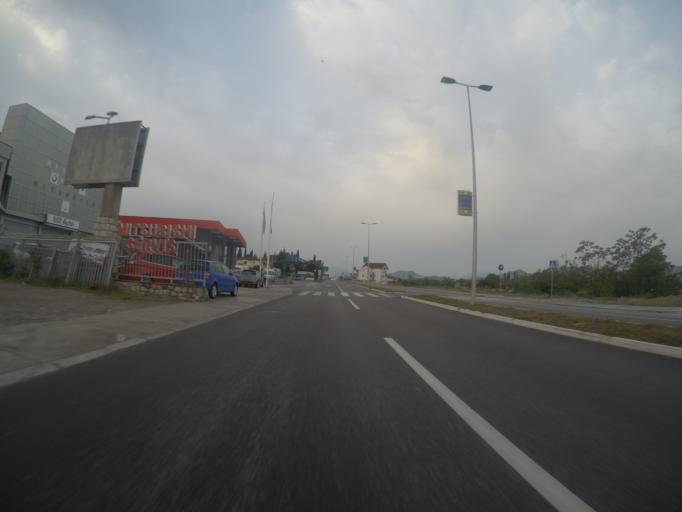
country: ME
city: Mojanovici
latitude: 42.3647
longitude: 19.2270
